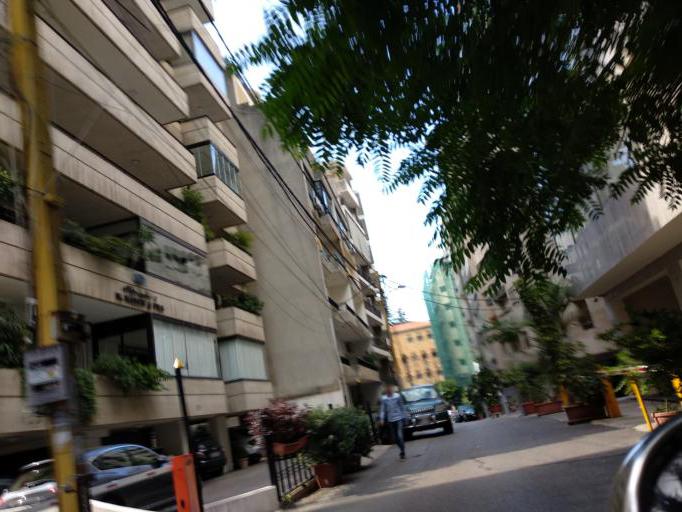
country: LB
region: Beyrouth
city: Beirut
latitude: 33.8871
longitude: 35.5234
